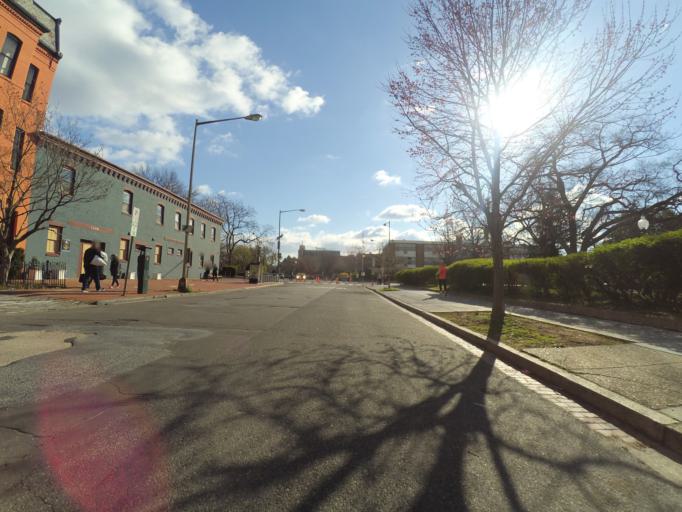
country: US
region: Washington, D.C.
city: Washington, D.C.
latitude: 38.8852
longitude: -77.0027
